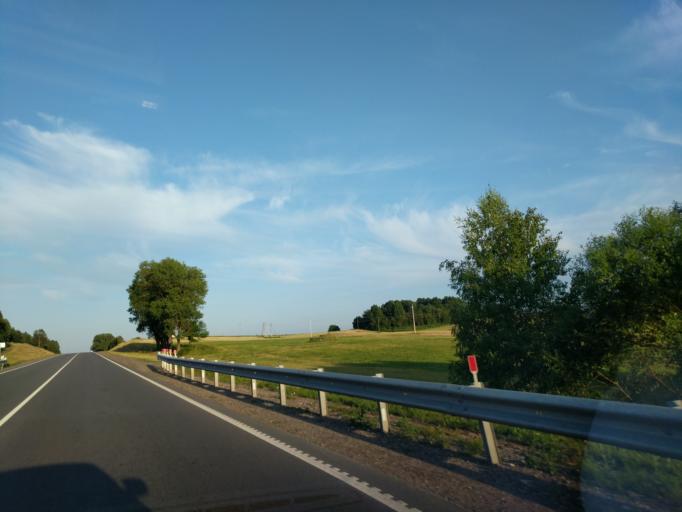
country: BY
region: Minsk
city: Syomkava
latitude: 54.1051
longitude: 27.4700
